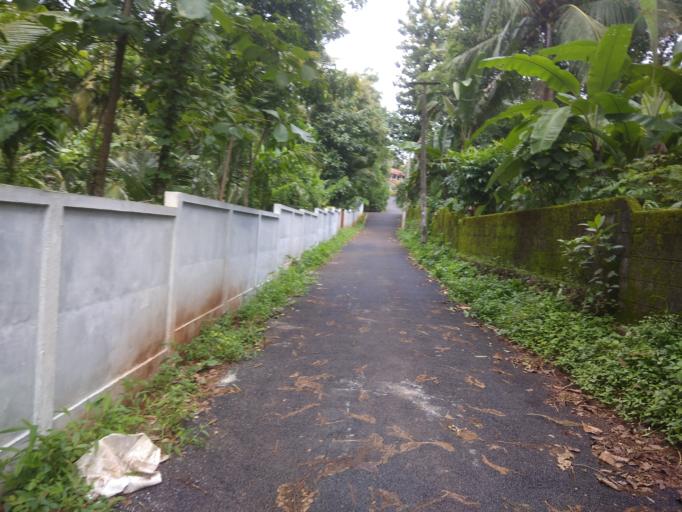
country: IN
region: Kerala
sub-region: Thrissur District
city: Avanoor
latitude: 10.5599
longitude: 76.1726
